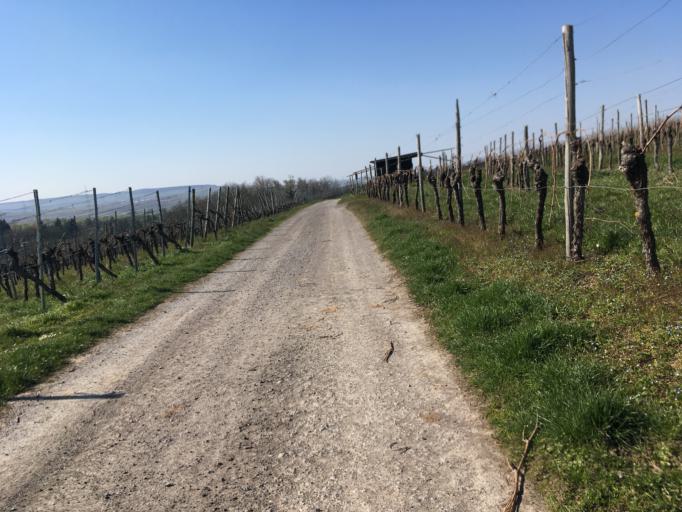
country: DE
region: Baden-Wuerttemberg
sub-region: Regierungsbezirk Stuttgart
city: Talheim
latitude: 49.0933
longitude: 9.1886
